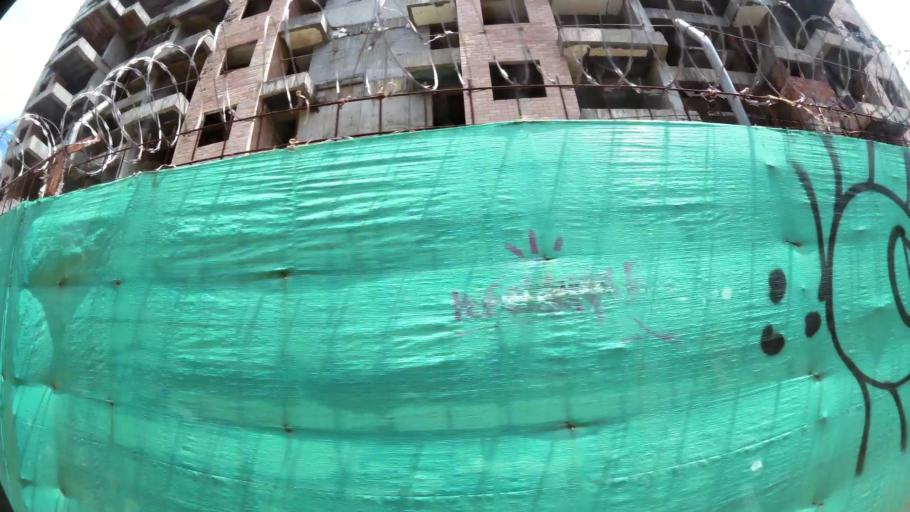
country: CO
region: Antioquia
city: La Estrella
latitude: 6.1567
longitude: -75.6298
